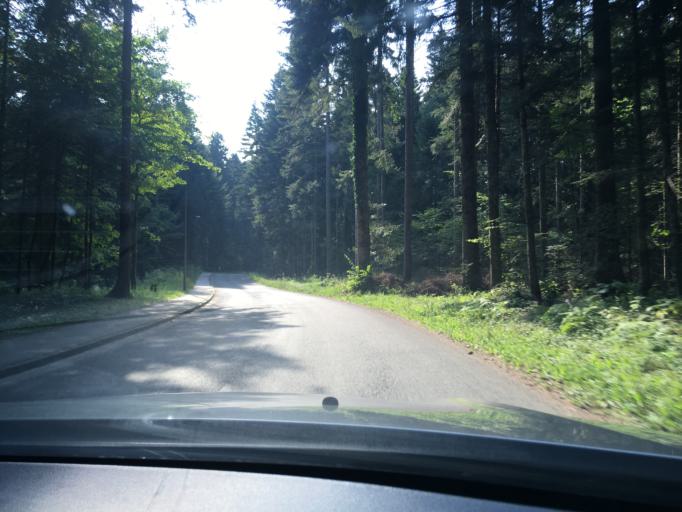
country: SI
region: Dolenjske Toplice
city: Dolenjske Toplice
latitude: 45.7600
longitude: 15.0511
